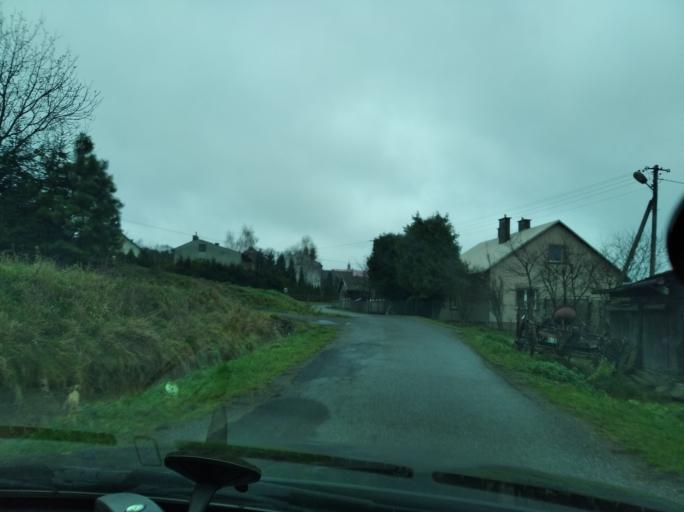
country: PL
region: Subcarpathian Voivodeship
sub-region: Powiat przeworski
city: Jawornik Polski
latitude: 49.8887
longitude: 22.2787
